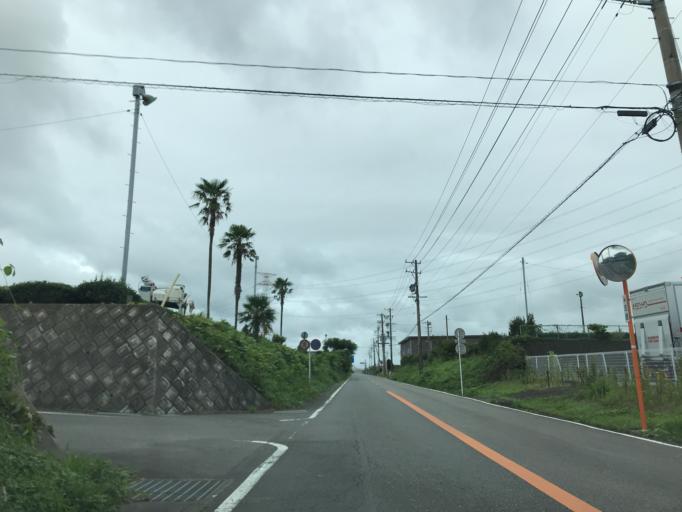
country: JP
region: Shizuoka
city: Kanaya
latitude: 34.7690
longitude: 138.1389
